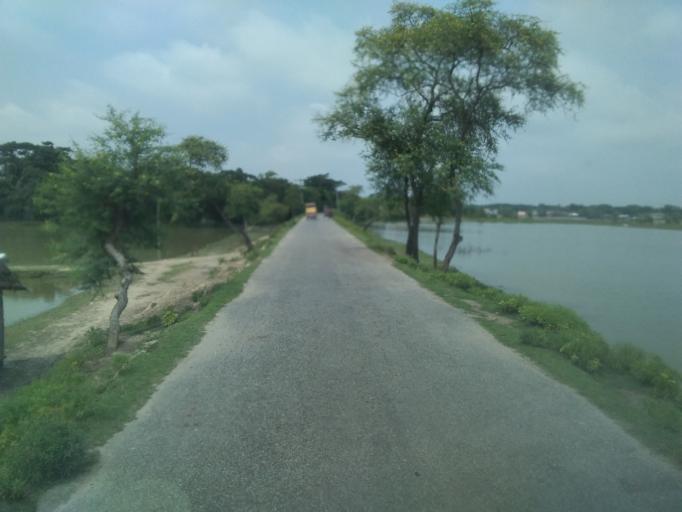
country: BD
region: Khulna
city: Phultala
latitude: 22.7042
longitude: 89.4588
